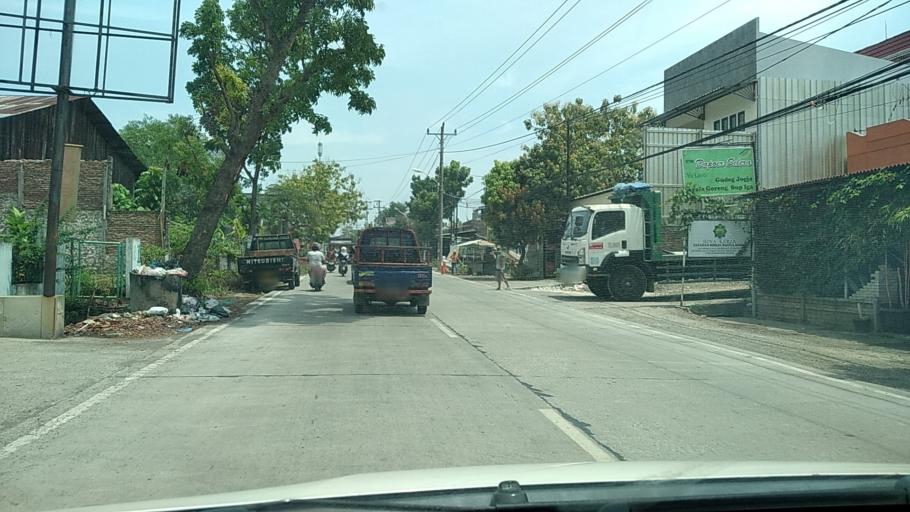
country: ID
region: Central Java
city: Mranggen
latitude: -7.0477
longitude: 110.4700
